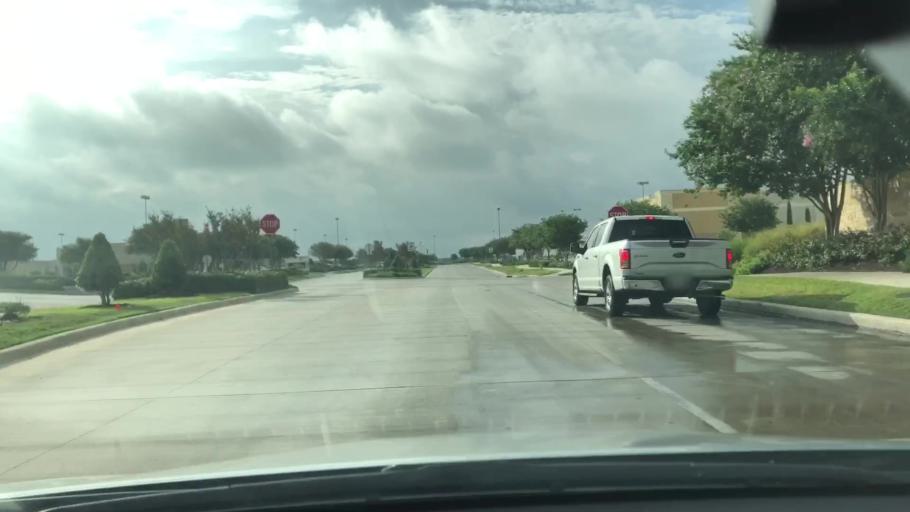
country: US
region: Texas
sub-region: Guadalupe County
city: Lake Dunlap
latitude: 29.7294
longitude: -98.0738
